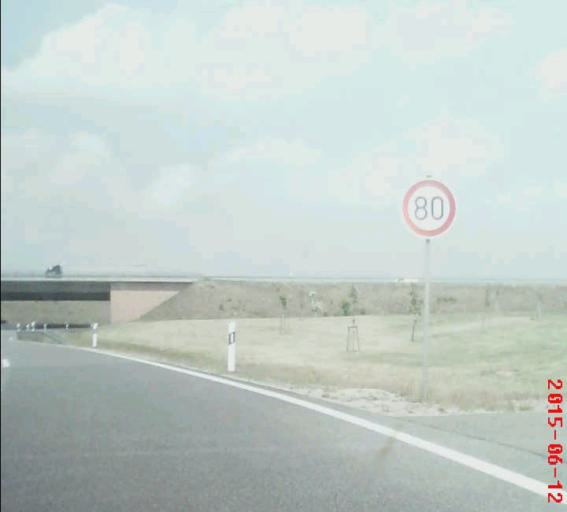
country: DE
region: Saxony-Anhalt
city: Oberroblingen
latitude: 51.4389
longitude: 11.3323
